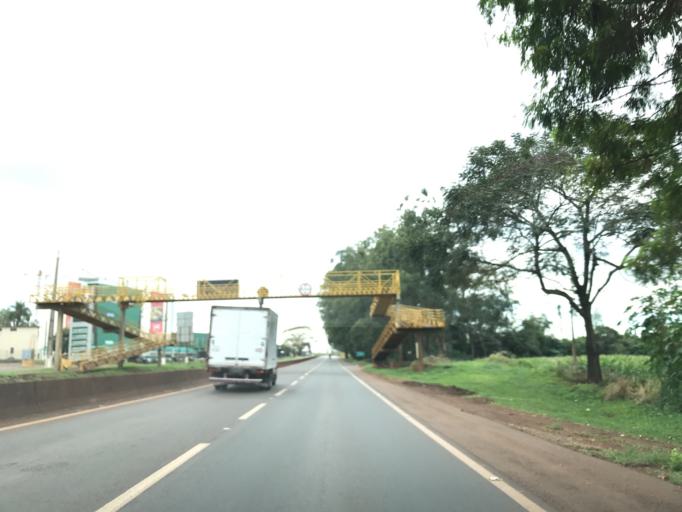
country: BR
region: Parana
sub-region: Rolandia
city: Rolandia
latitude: -23.3567
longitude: -51.3945
